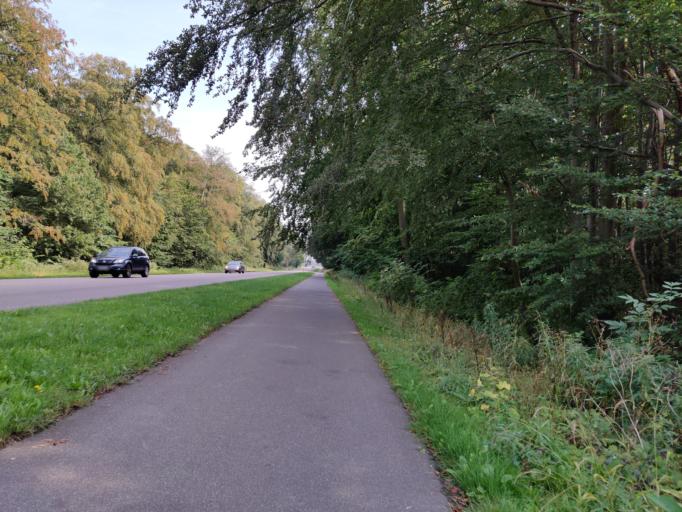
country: DK
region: Zealand
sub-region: Guldborgsund Kommune
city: Nykobing Falster
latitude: 54.7514
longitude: 11.9025
